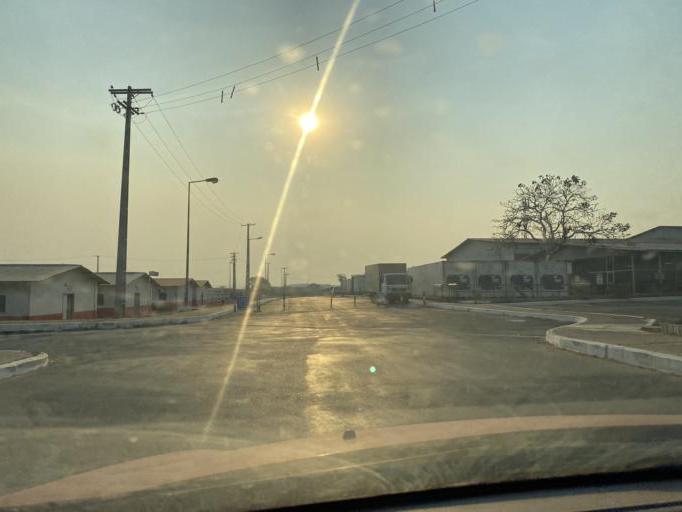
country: AO
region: Cuanza Norte
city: N'dalatando
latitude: -9.7407
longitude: 15.1407
